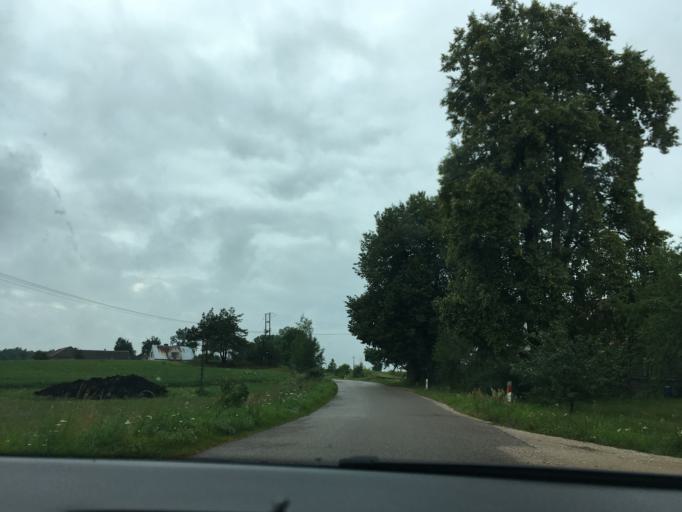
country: PL
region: Podlasie
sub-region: Powiat sejnenski
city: Krasnopol
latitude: 54.0962
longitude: 23.2306
